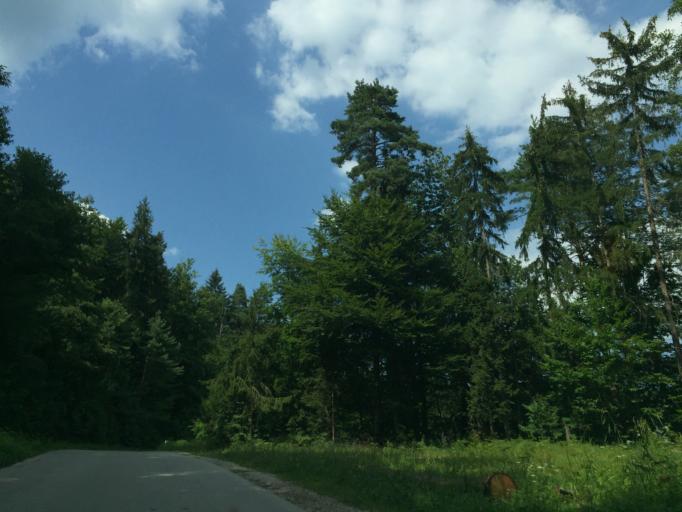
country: SI
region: Sostanj
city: Ravne
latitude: 46.3959
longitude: 15.0871
